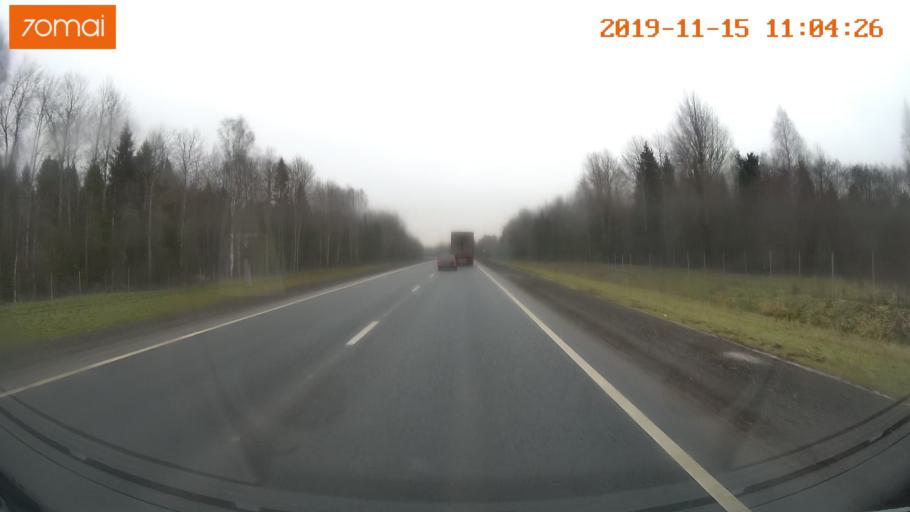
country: RU
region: Vologda
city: Chebsara
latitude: 59.1200
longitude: 38.9843
